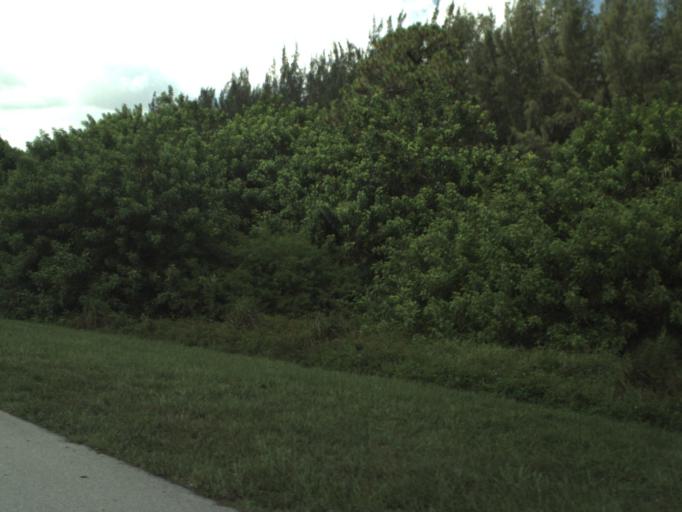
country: US
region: Florida
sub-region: Palm Beach County
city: Jupiter
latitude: 26.8964
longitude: -80.0949
